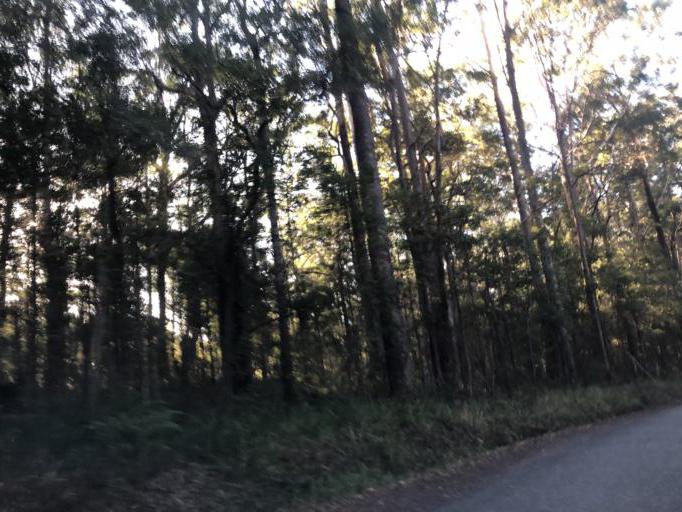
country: AU
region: New South Wales
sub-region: Nambucca Shire
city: Nambucca
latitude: -30.6083
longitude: 152.9744
